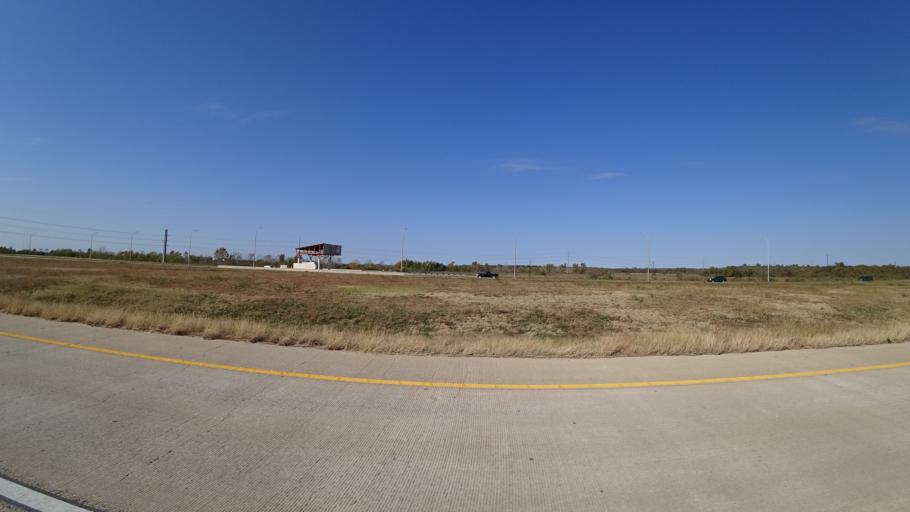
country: US
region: Texas
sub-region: Travis County
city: Hornsby Bend
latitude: 30.2473
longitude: -97.6082
